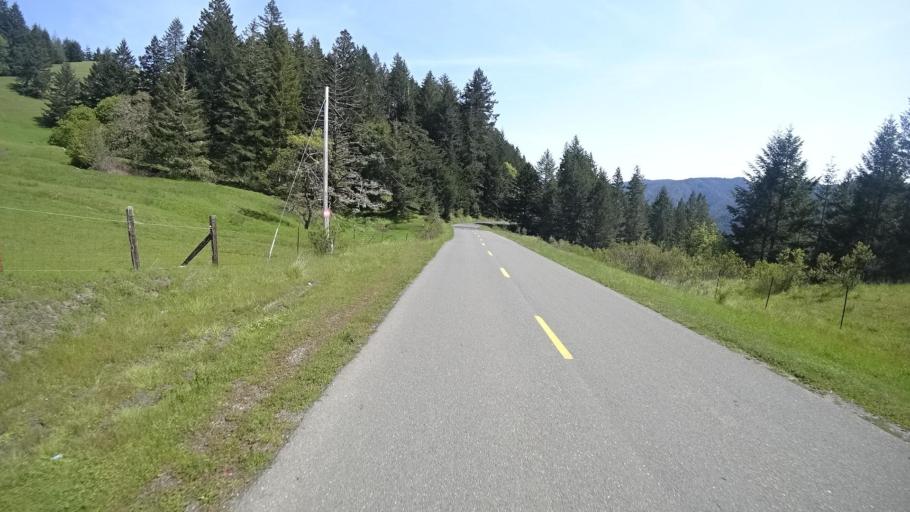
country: US
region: California
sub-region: Humboldt County
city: Redway
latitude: 40.4115
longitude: -123.7569
